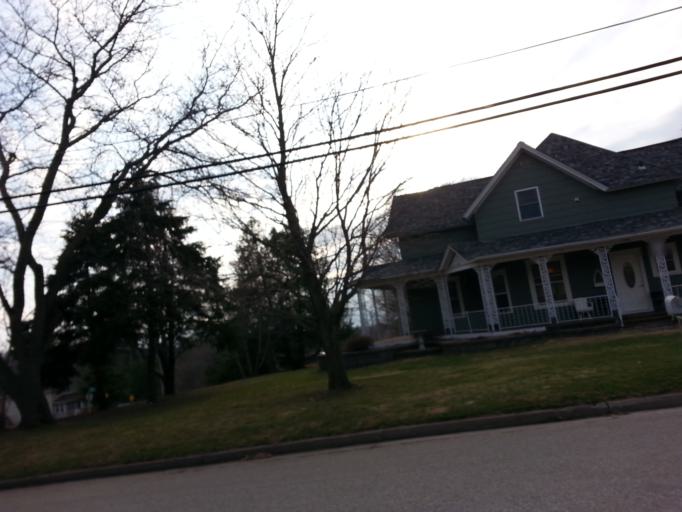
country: US
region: Wisconsin
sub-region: Pierce County
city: Ellsworth
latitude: 44.7323
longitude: -92.4909
